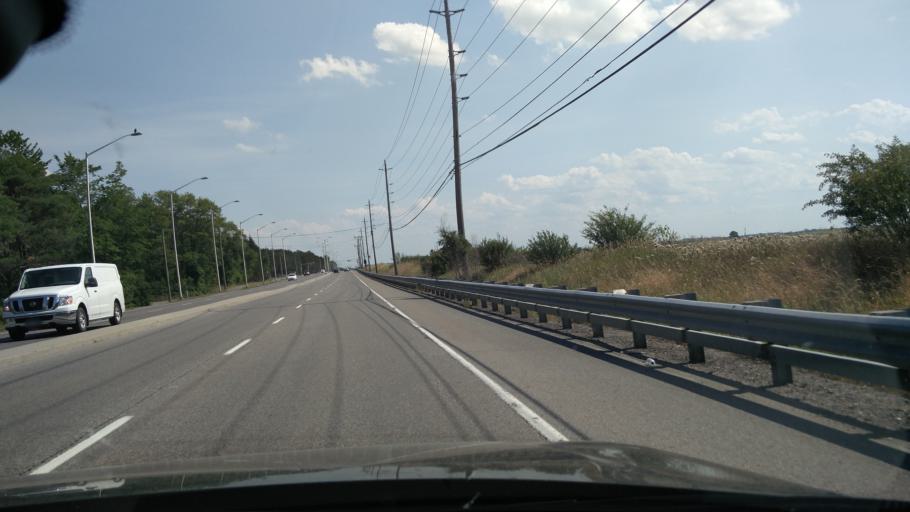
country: CA
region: Ontario
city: Bells Corners
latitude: 45.3210
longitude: -75.7443
